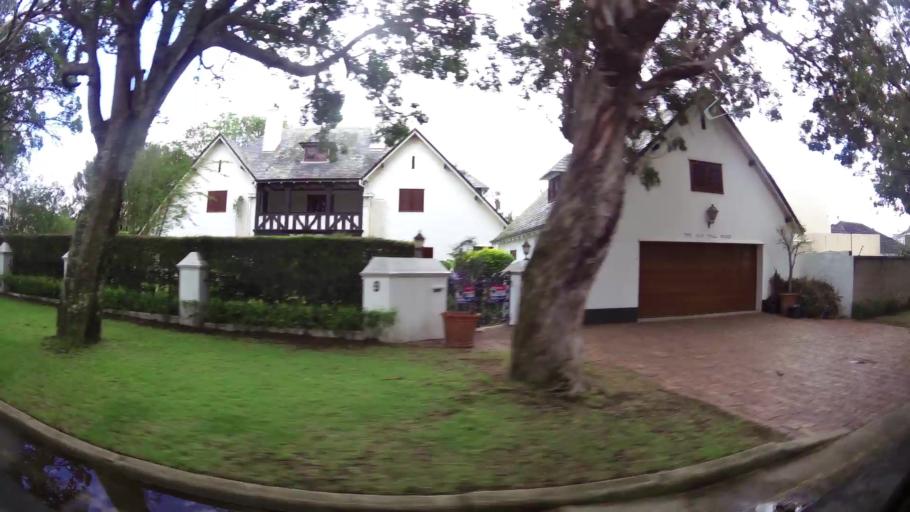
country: ZA
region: Eastern Cape
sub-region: Nelson Mandela Bay Metropolitan Municipality
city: Port Elizabeth
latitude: -33.9658
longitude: 25.5949
